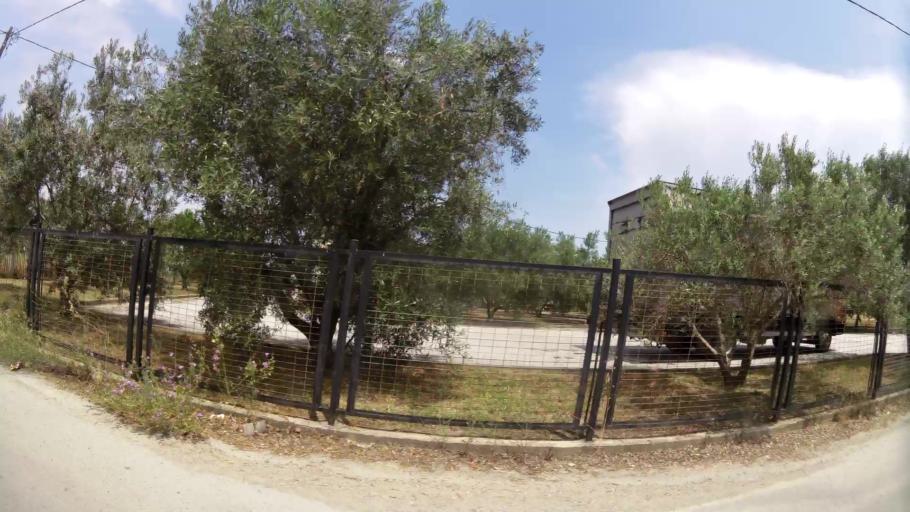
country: GR
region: Central Macedonia
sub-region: Nomos Pierias
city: Peristasi
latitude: 40.2717
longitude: 22.5473
